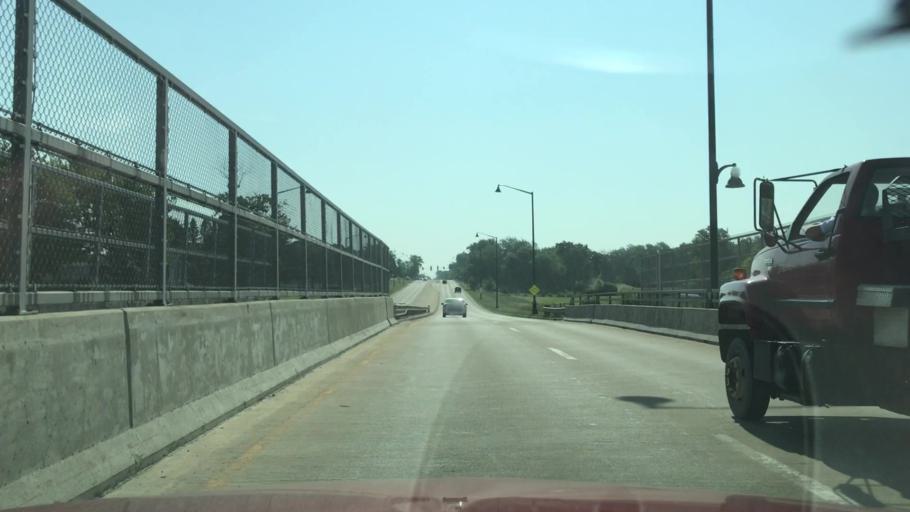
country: US
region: Illinois
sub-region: Winnebago County
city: Rockford
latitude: 42.2379
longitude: -89.0515
